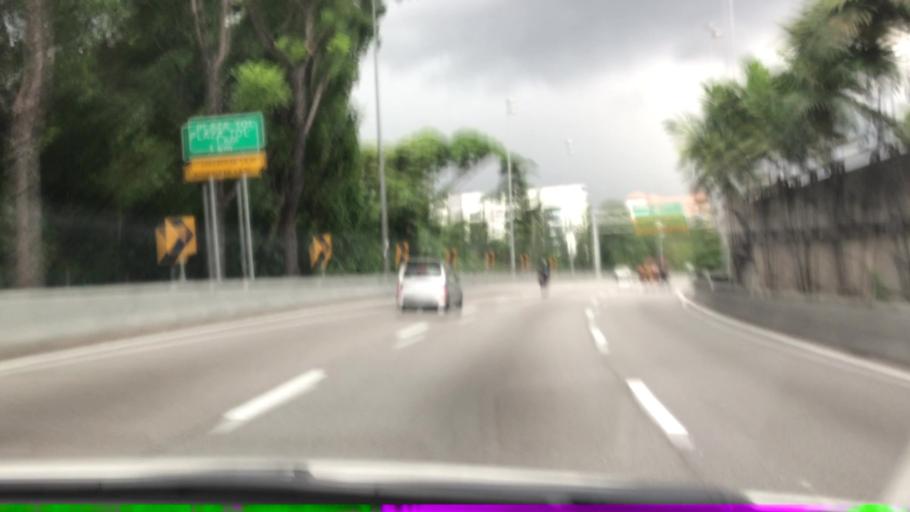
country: MY
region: Kuala Lumpur
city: Kuala Lumpur
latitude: 3.1205
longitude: 101.6613
